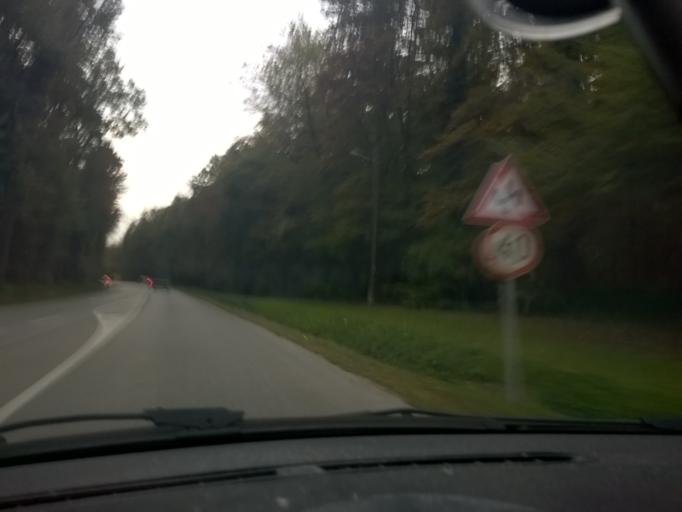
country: HR
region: Zagrebacka
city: Brdovec
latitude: 45.8799
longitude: 15.7991
